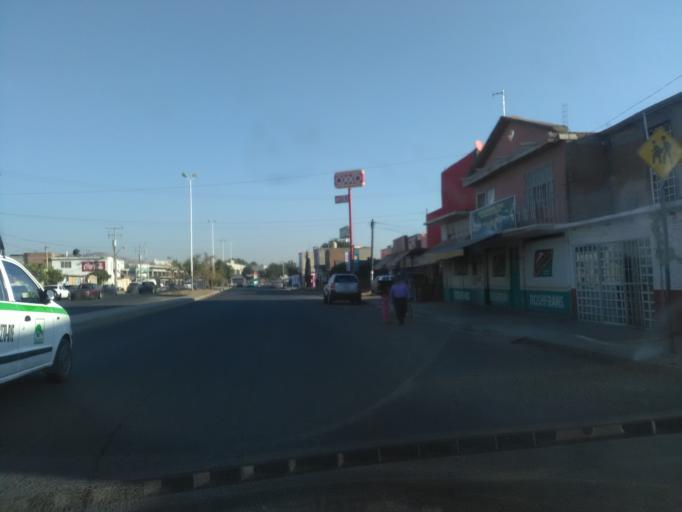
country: MX
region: Durango
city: Victoria de Durango
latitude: 24.0522
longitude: -104.6424
